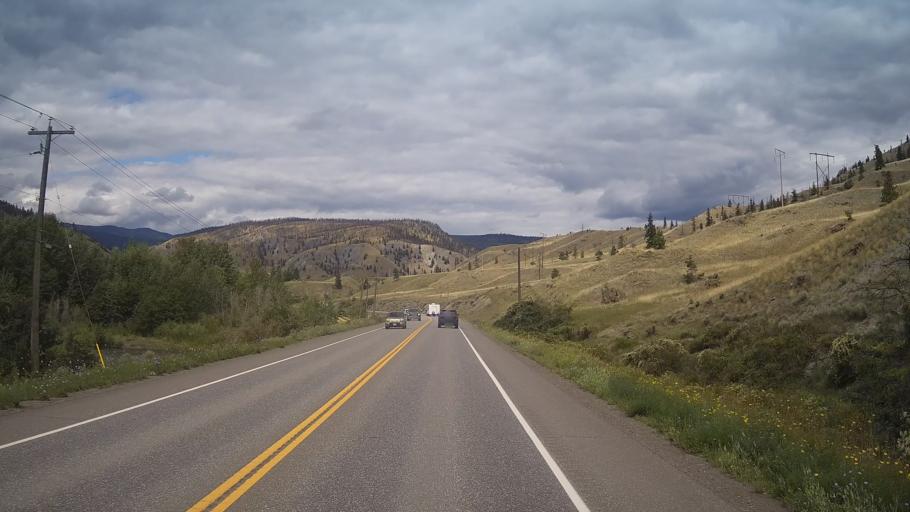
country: CA
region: British Columbia
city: Cache Creek
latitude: 50.9588
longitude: -121.4449
